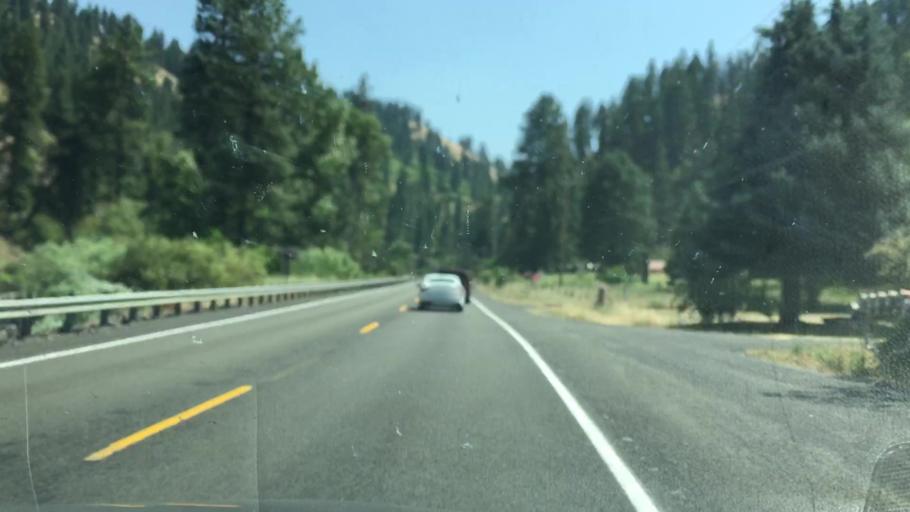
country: US
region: Idaho
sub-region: Valley County
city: McCall
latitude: 45.2386
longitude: -116.3301
